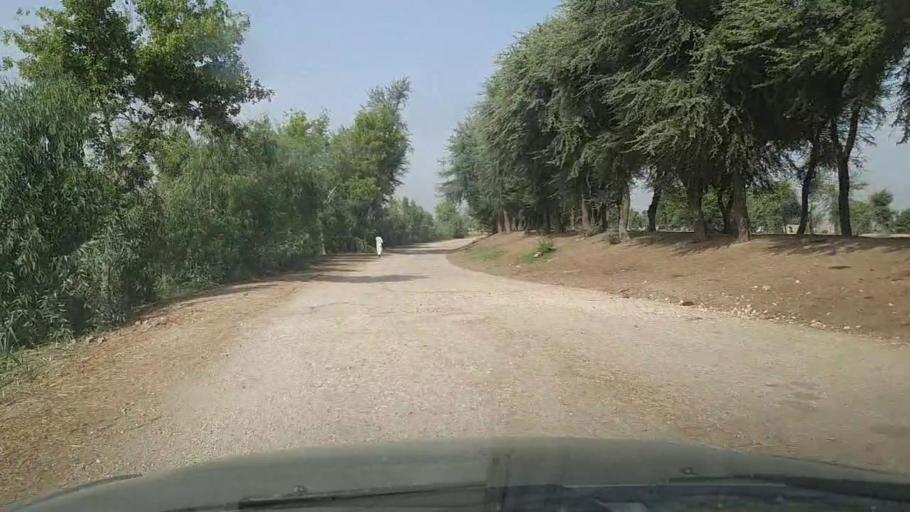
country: PK
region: Sindh
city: Pir jo Goth
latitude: 27.5165
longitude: 68.4767
